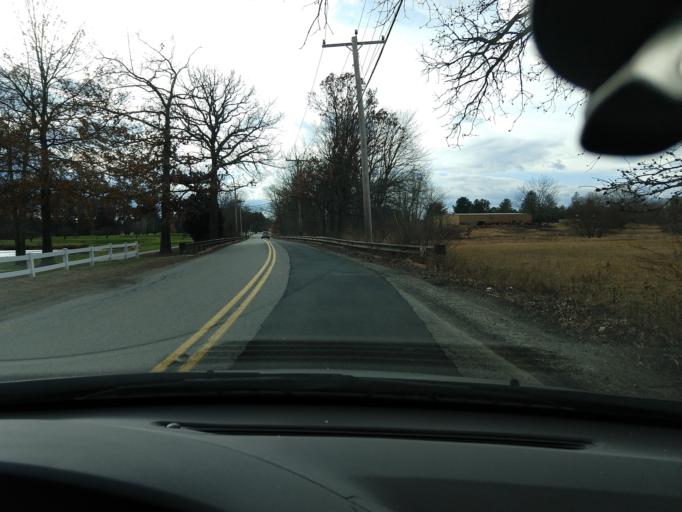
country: US
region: Massachusetts
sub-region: Middlesex County
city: West Concord
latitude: 42.4180
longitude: -71.3735
